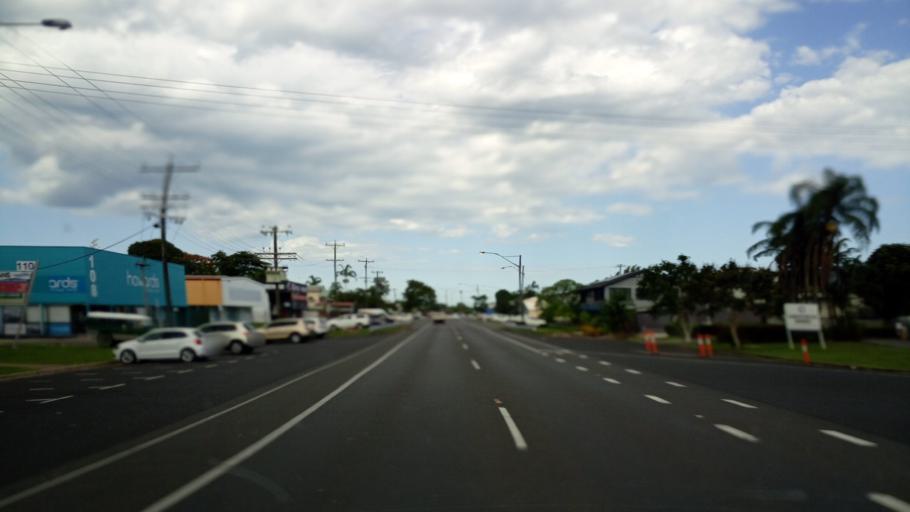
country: AU
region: Queensland
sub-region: Cairns
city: Cairns
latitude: -16.9342
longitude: 145.7599
